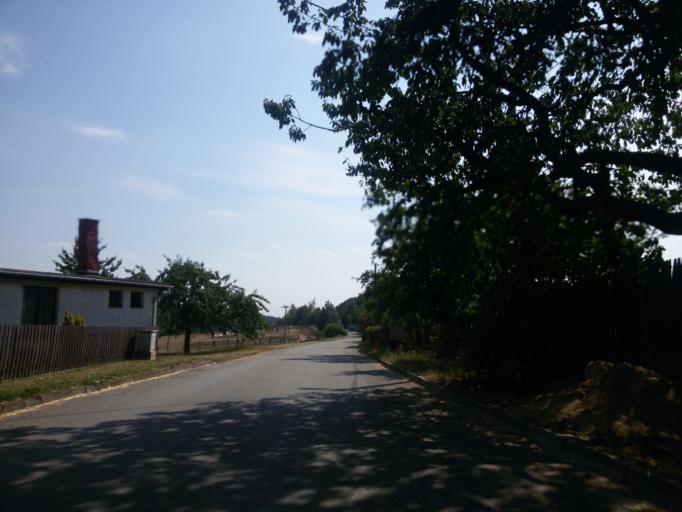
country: CZ
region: South Moravian
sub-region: Okres Brno-Venkov
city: Lomnice
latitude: 49.4424
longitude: 16.4565
